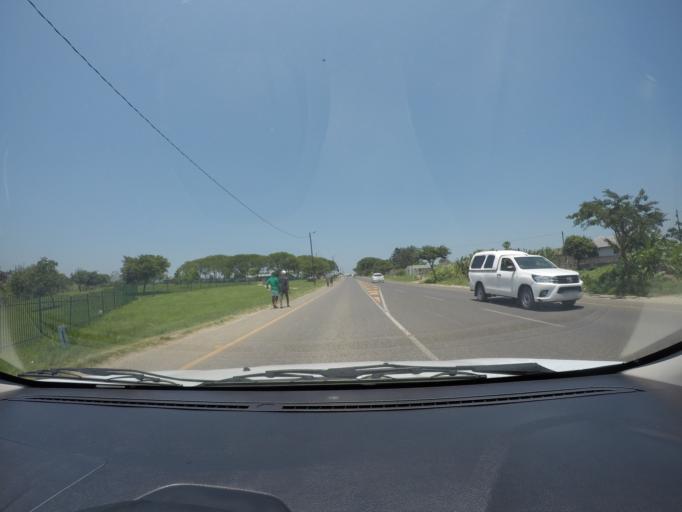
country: ZA
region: KwaZulu-Natal
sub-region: uThungulu District Municipality
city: eSikhawini
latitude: -28.8777
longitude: 31.9023
